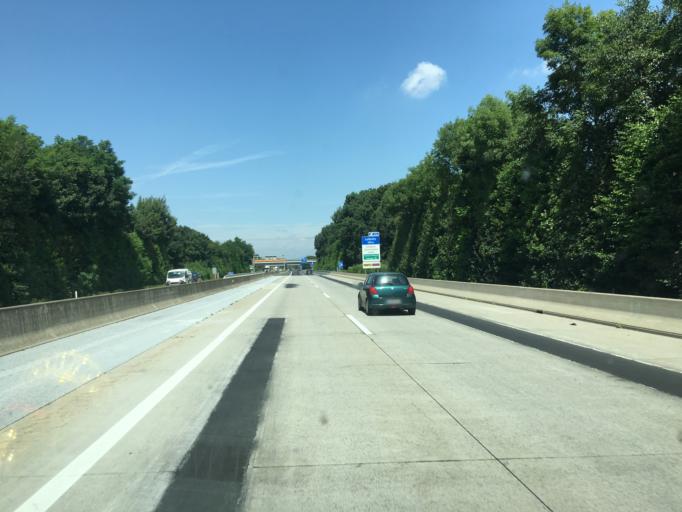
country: AT
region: Styria
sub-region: Politischer Bezirk Leibnitz
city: Gabersdorf
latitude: 46.8014
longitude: 15.5704
